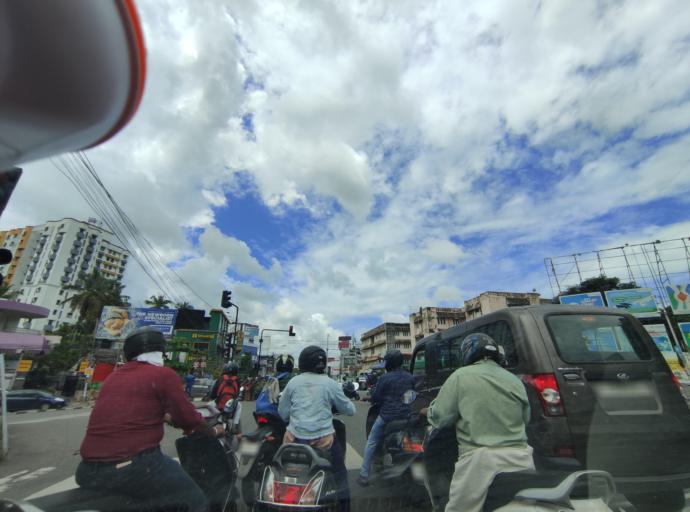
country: IN
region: Kerala
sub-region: Thiruvananthapuram
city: Thiruvananthapuram
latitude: 8.5188
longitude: 76.9423
